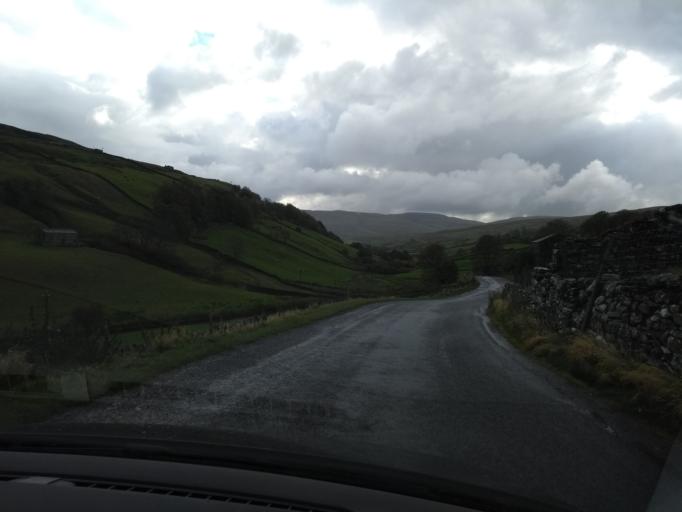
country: GB
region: England
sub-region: County Durham
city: Bowes
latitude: 54.4024
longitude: -2.1664
